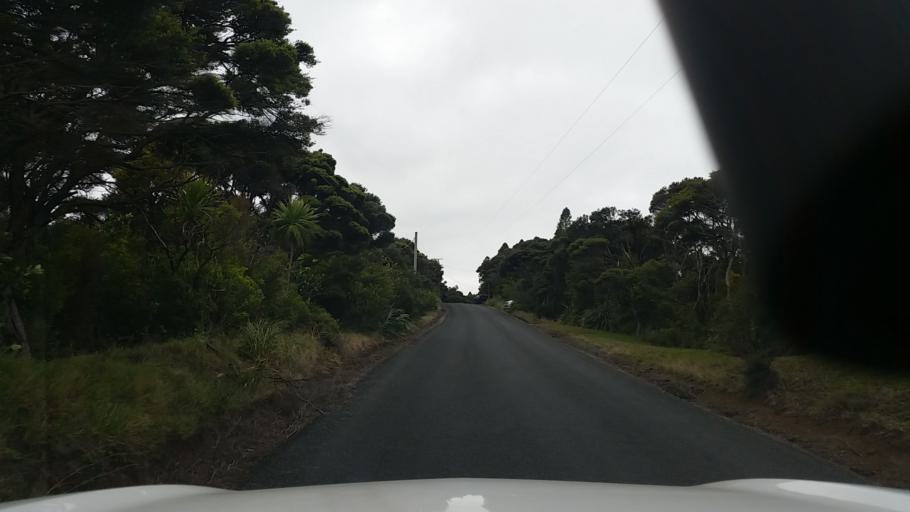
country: NZ
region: Auckland
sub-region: Auckland
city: Muriwai Beach
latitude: -36.8762
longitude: 174.4776
